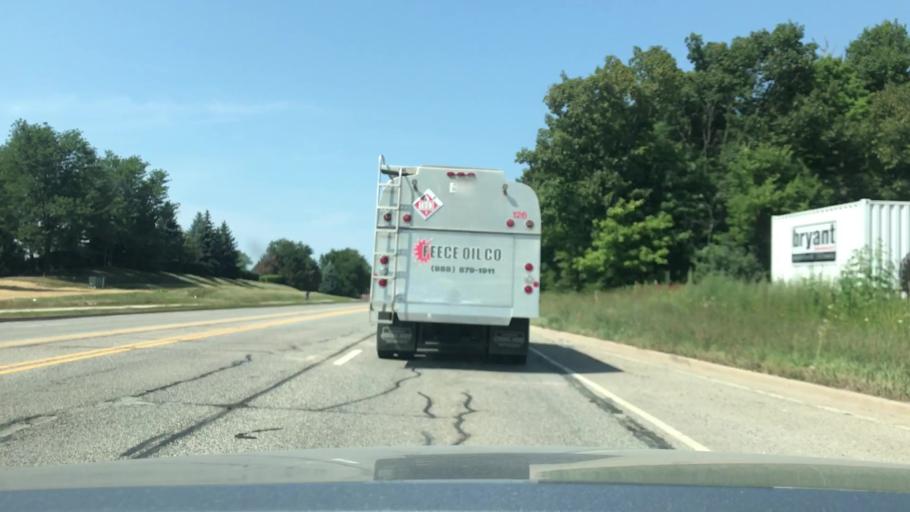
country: US
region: Illinois
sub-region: Kane County
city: Batavia
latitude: 41.8216
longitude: -88.2798
